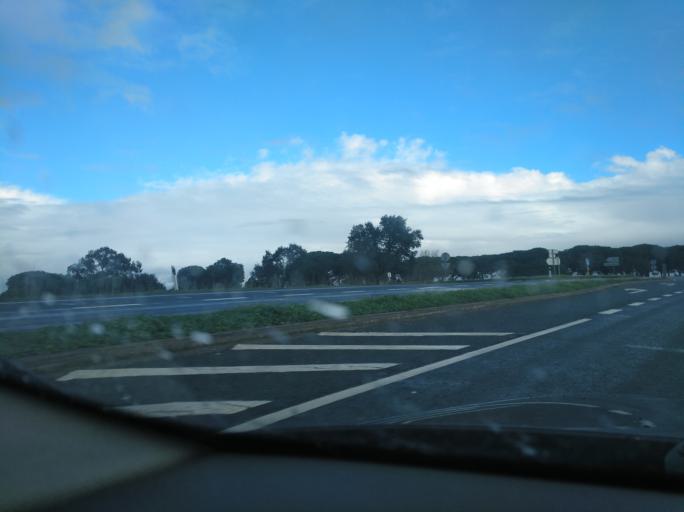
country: PT
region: Beja
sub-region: Aljustrel
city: Aljustrel
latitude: 38.0096
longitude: -8.3790
